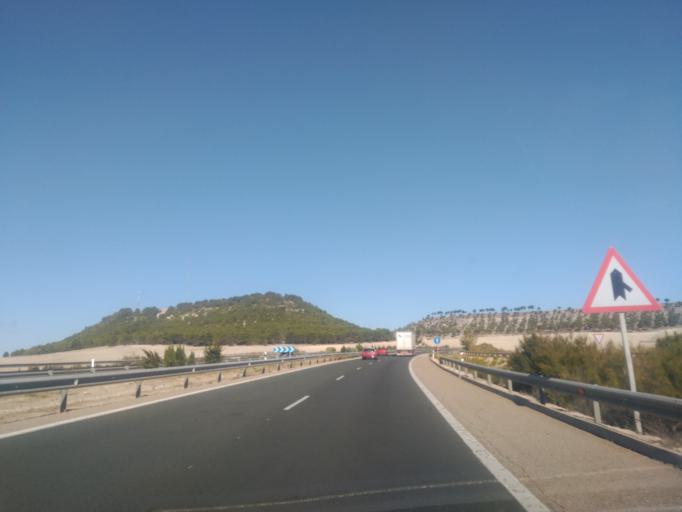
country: ES
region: Castille and Leon
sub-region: Provincia de Valladolid
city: Cisterniga
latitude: 41.6024
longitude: -4.6620
